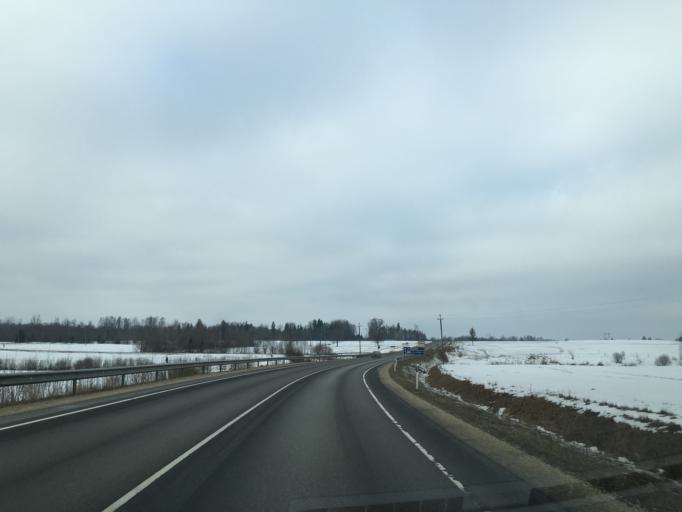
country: EE
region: Tartu
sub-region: Elva linn
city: Elva
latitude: 58.1597
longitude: 26.3034
